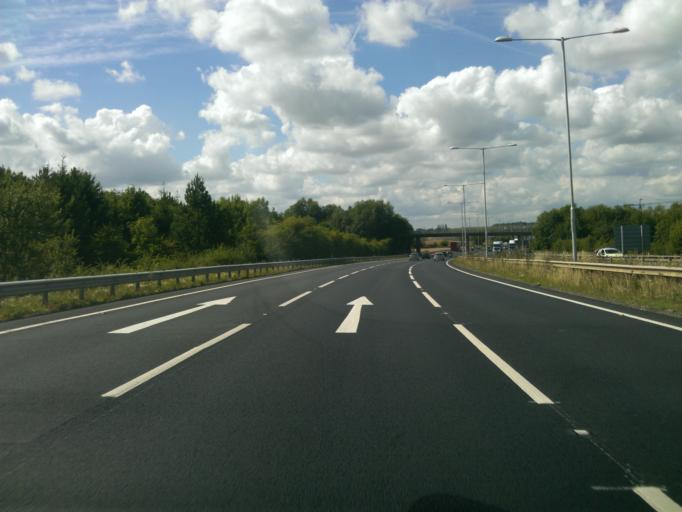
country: GB
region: England
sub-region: Northamptonshire
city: Kettering
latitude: 52.3742
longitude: -0.7223
